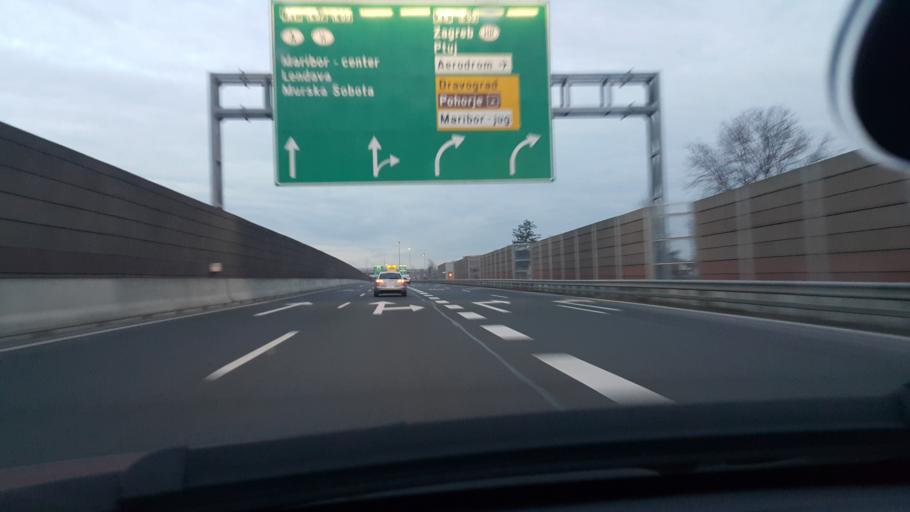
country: SI
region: Hoce-Slivnica
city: Radizel
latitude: 46.4733
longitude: 15.6581
